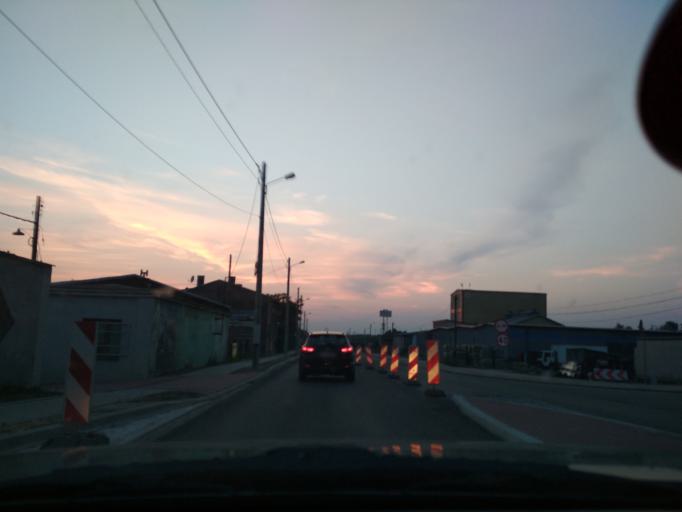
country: PL
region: Silesian Voivodeship
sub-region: Powiat zawiercianski
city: Ogrodzieniec
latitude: 50.4630
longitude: 19.4939
